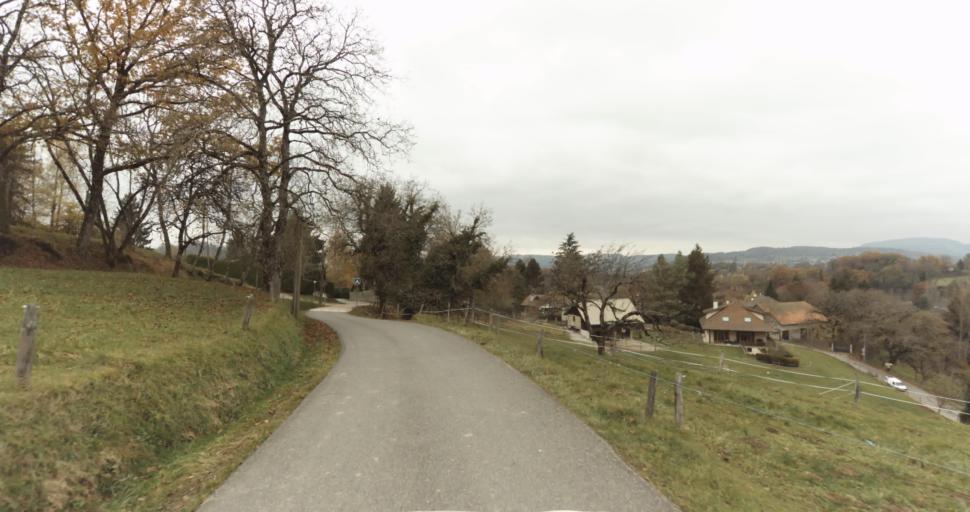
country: FR
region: Rhone-Alpes
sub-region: Departement de la Haute-Savoie
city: Chavanod
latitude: 45.8743
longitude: 6.0364
